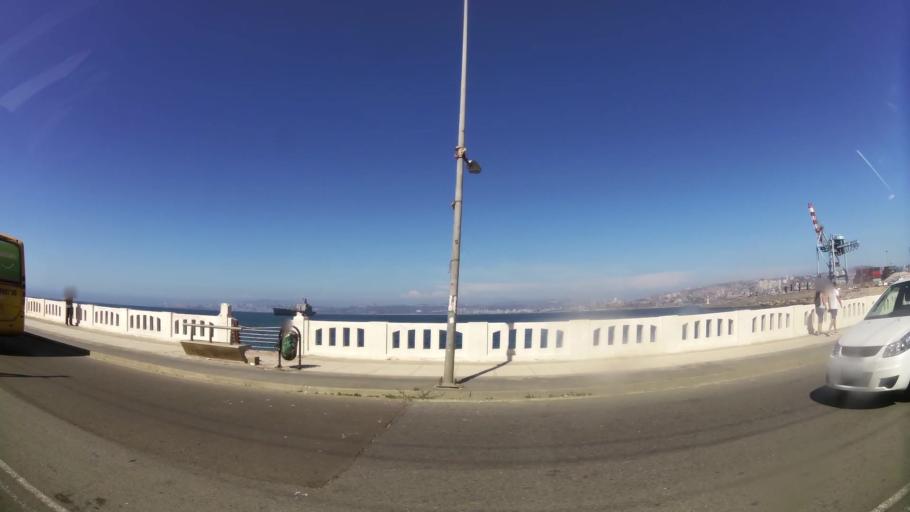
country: CL
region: Valparaiso
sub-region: Provincia de Valparaiso
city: Valparaiso
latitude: -33.0259
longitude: -71.6316
